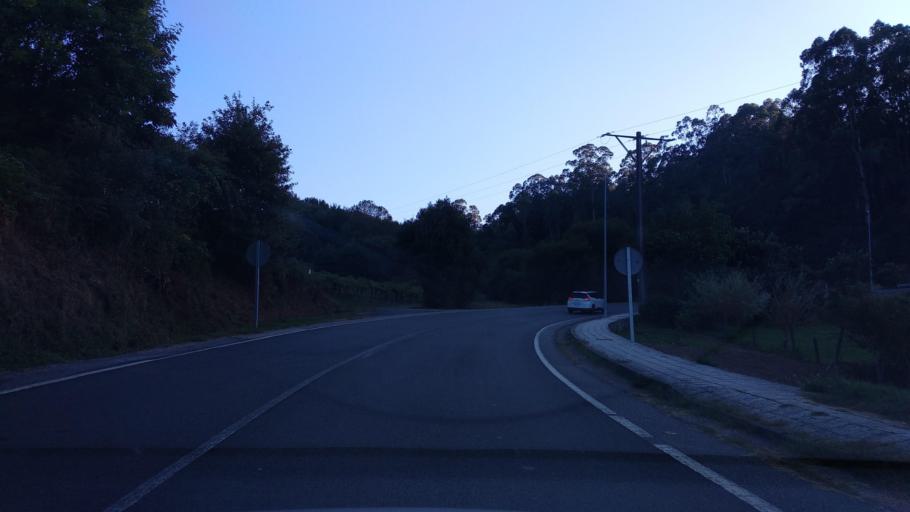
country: ES
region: Galicia
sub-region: Provincia de Pontevedra
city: Redondela
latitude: 42.3346
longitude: -8.5801
